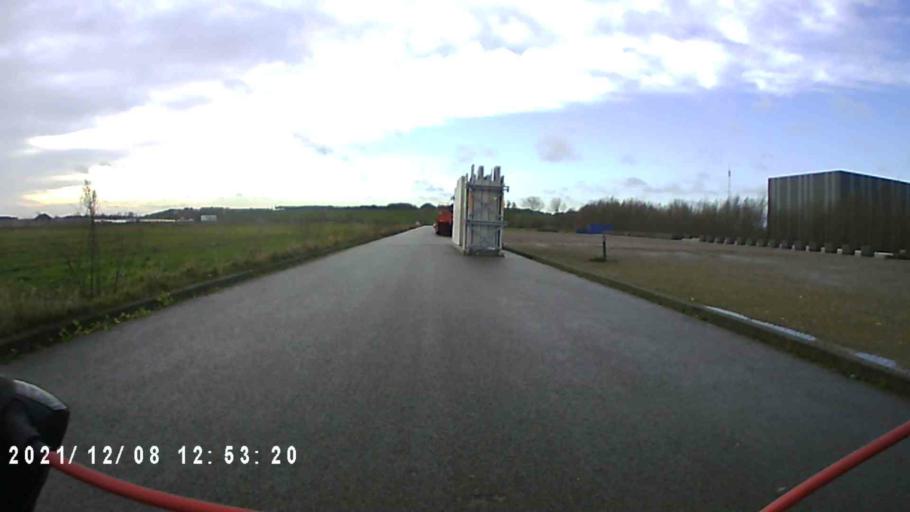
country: NL
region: Groningen
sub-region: Gemeente Haren
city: Haren
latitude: 53.2025
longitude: 6.6322
